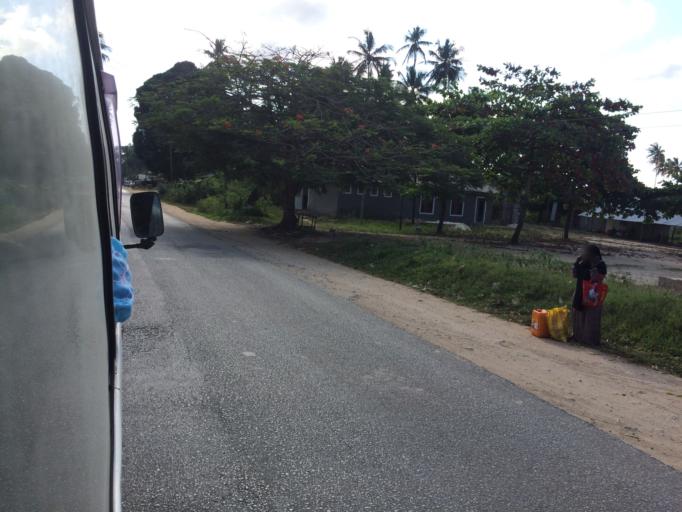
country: TZ
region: Zanzibar Central/South
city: Koani
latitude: -6.1956
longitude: 39.2969
